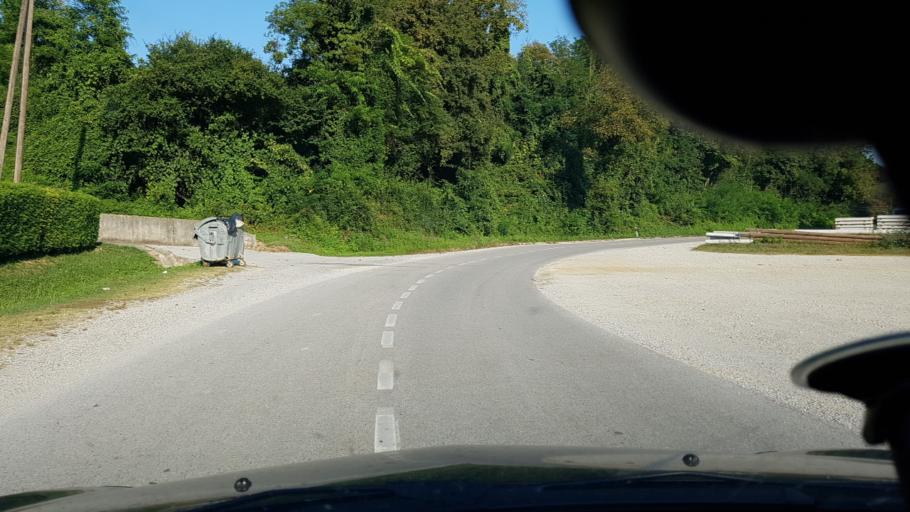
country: SI
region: Bistrica ob Sotli
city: Bistrica ob Sotli
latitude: 46.0493
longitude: 15.7514
